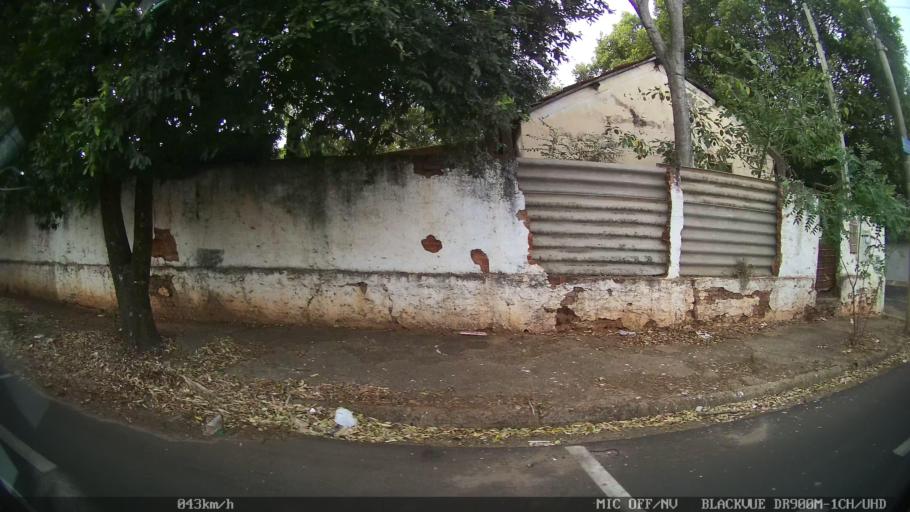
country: BR
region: Sao Paulo
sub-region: Catanduva
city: Catanduva
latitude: -21.1227
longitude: -48.9671
